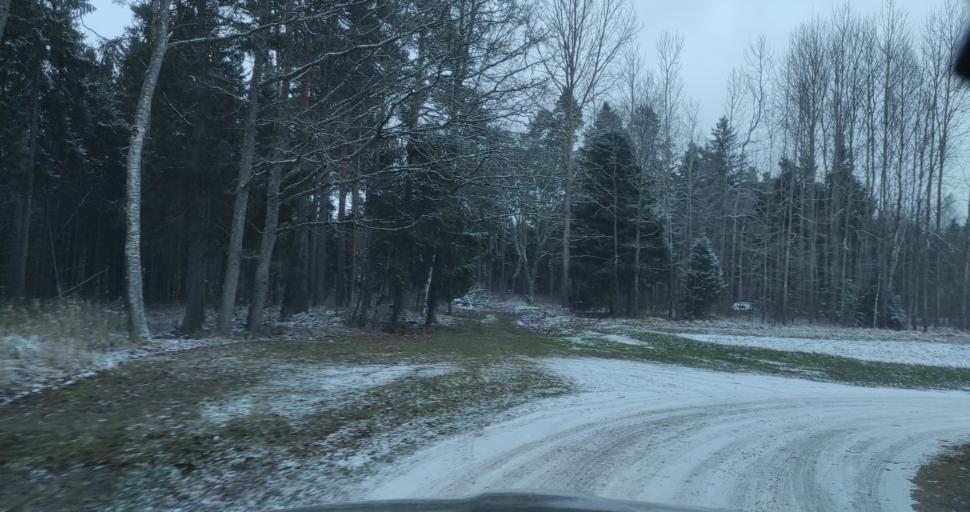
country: LV
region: Kuldigas Rajons
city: Kuldiga
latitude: 56.9782
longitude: 22.0321
